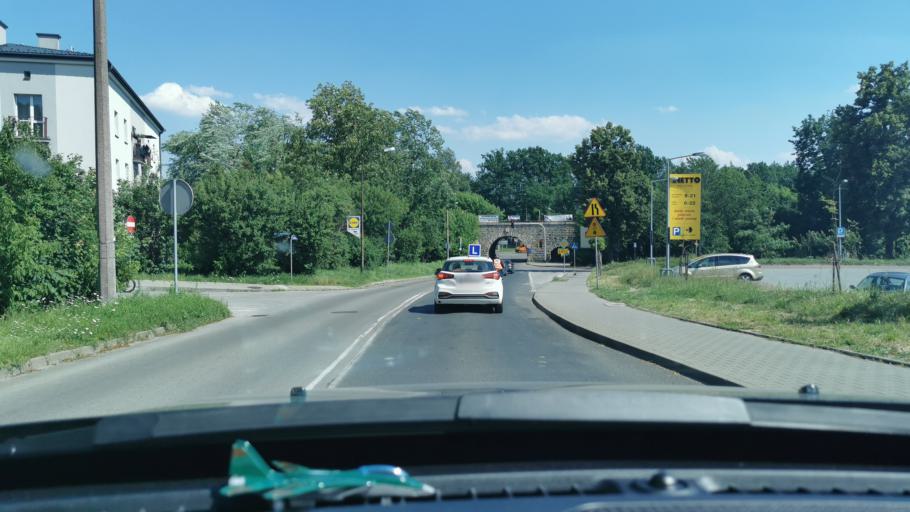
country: PL
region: Lesser Poland Voivodeship
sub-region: Powiat chrzanowski
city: Chrzanow
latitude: 50.1363
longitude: 19.4006
